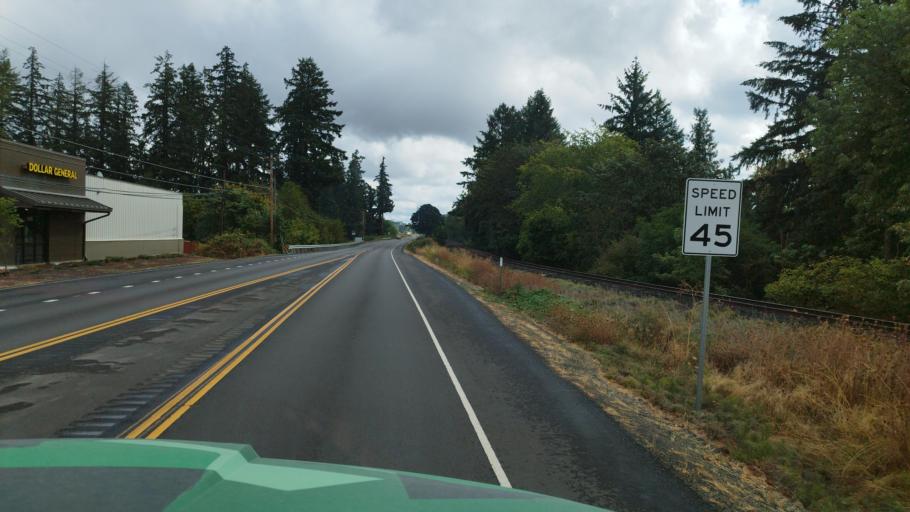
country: US
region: Oregon
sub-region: Yamhill County
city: Lafayette
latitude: 45.2421
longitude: -123.1039
